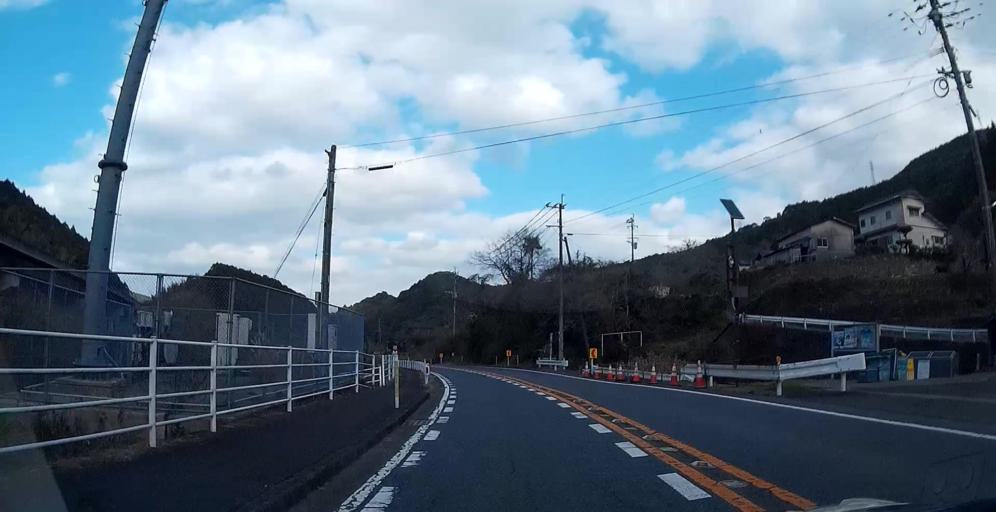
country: JP
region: Kumamoto
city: Yatsushiro
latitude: 32.3834
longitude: 130.5413
